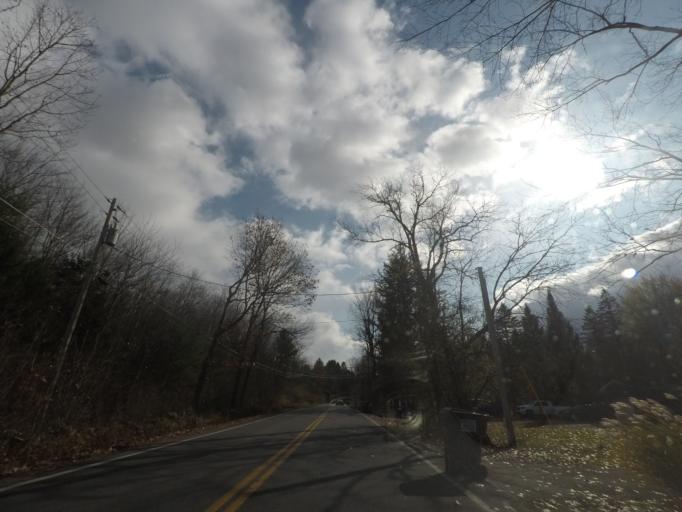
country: US
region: New York
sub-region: Saratoga County
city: Country Knolls
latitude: 42.9426
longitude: -73.8529
